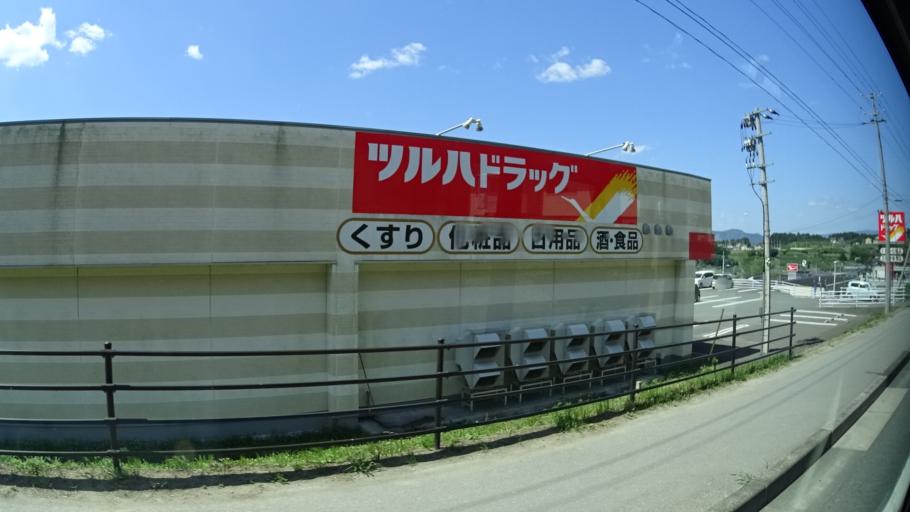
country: JP
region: Iwate
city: Ofunato
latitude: 39.0107
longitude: 141.6744
